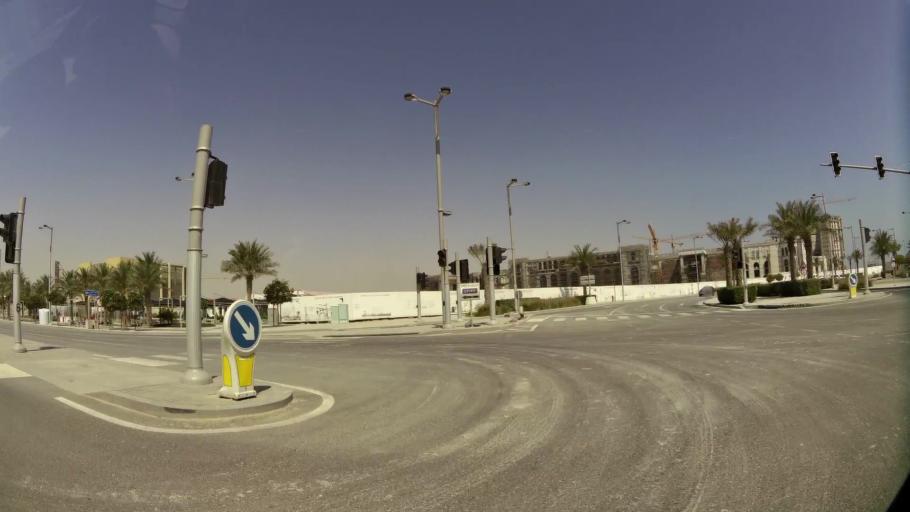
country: QA
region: Baladiyat Umm Salal
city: Umm Salal Muhammad
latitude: 25.3994
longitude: 51.5219
